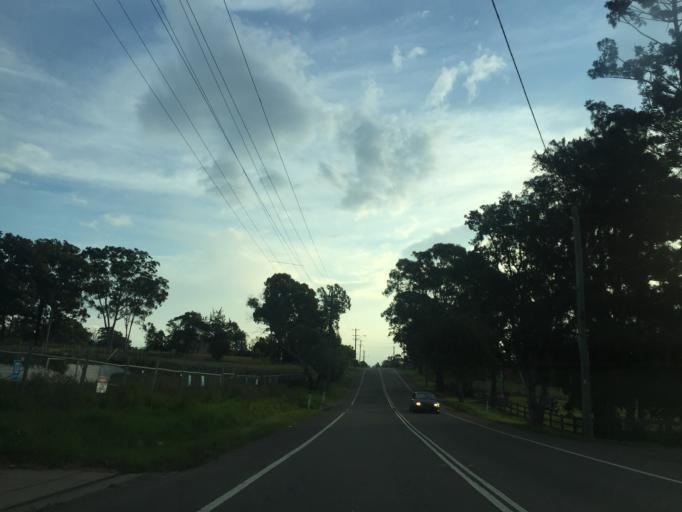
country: AU
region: New South Wales
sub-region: The Hills Shire
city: Beaumont Hills
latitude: -33.7177
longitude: 150.9476
